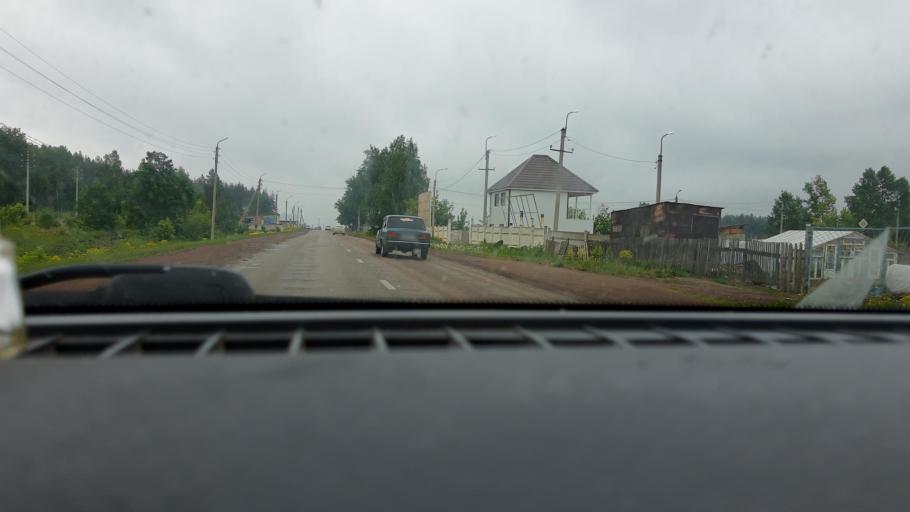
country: RU
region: Bashkortostan
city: Belebey
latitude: 54.0809
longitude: 54.0890
